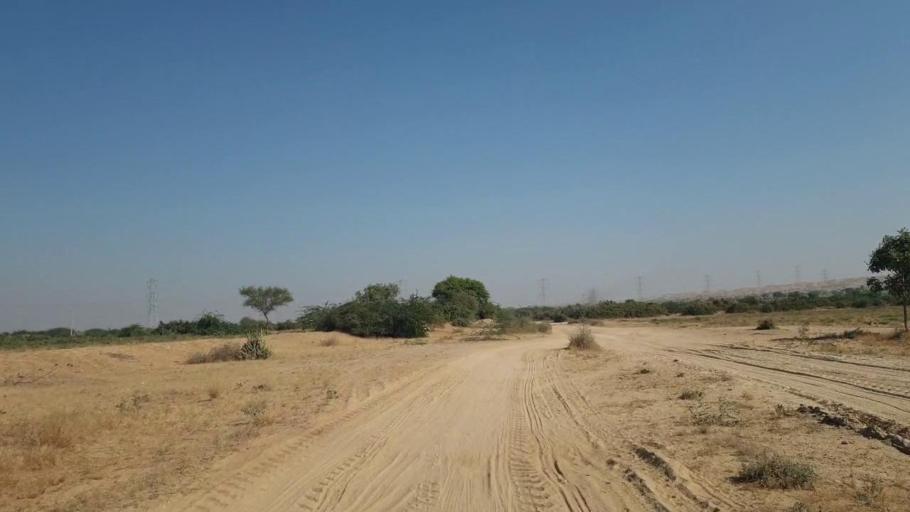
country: PK
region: Sindh
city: Gharo
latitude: 25.1902
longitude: 67.7399
